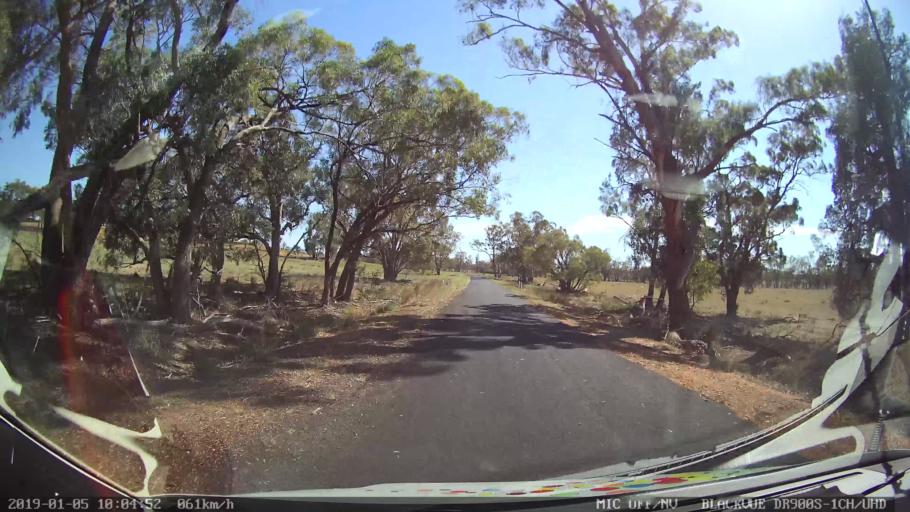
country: AU
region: New South Wales
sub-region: Gilgandra
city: Gilgandra
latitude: -31.6713
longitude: 148.8623
